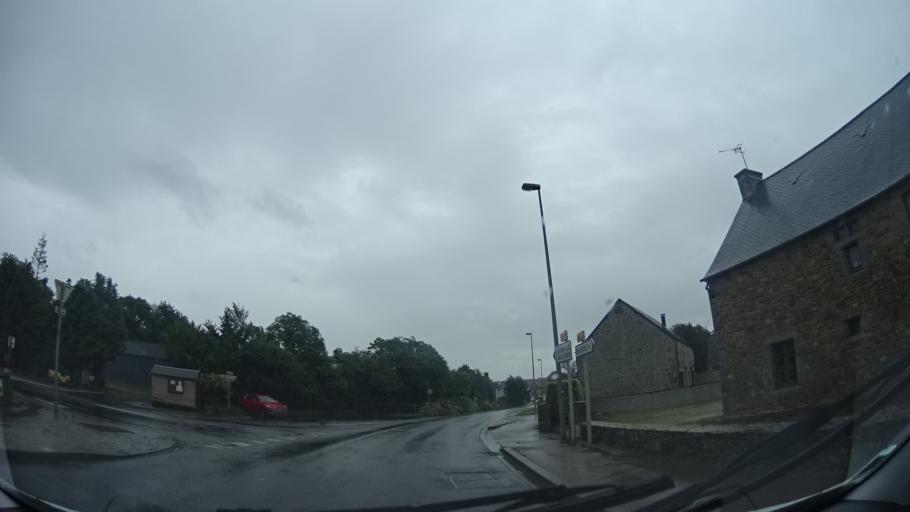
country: FR
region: Lower Normandy
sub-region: Departement de la Manche
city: Urville-Nacqueville
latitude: 49.5990
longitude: -1.7800
